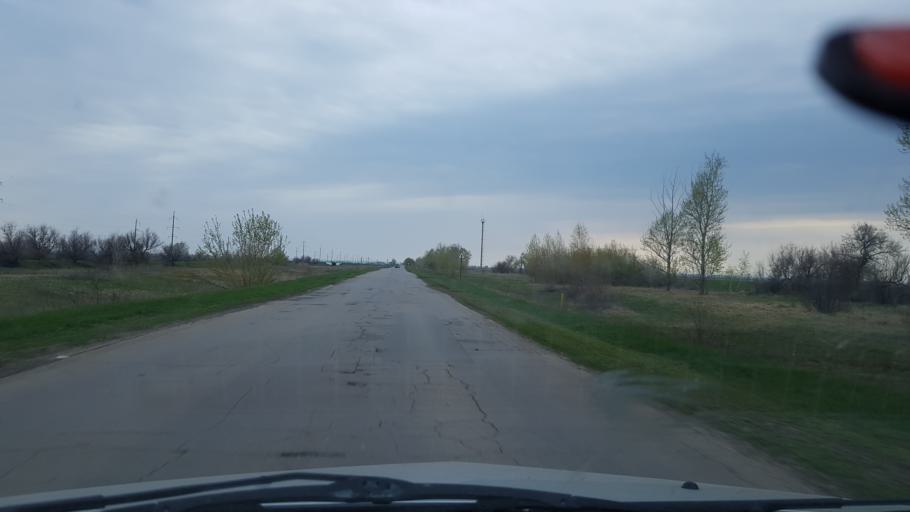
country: RU
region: Samara
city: Khryashchevka
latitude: 53.6687
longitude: 49.1337
